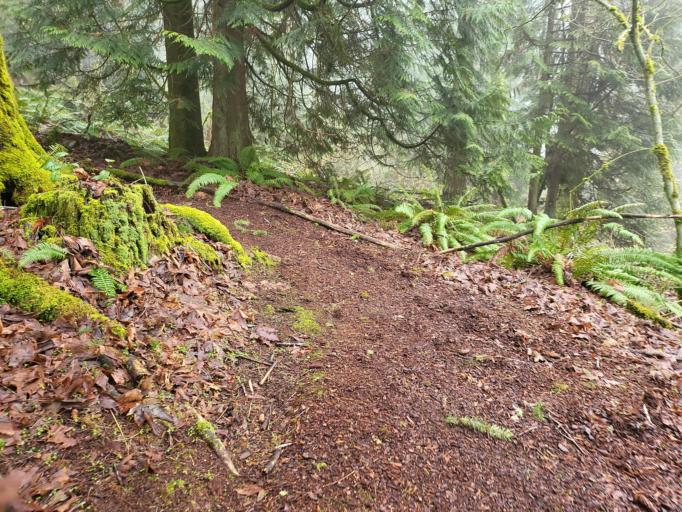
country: US
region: Washington
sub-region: King County
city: Newcastle
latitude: 47.5398
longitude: -122.1284
